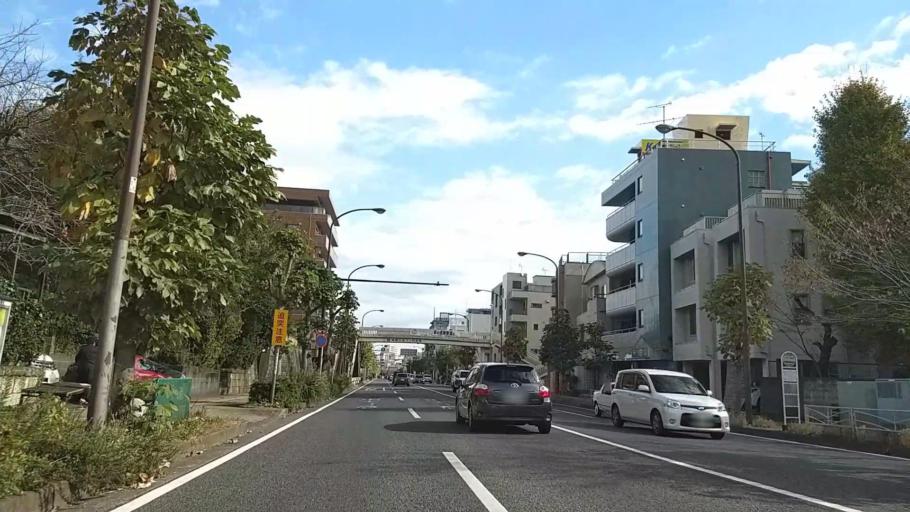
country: JP
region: Kanagawa
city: Yokohama
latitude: 35.4765
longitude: 139.6079
